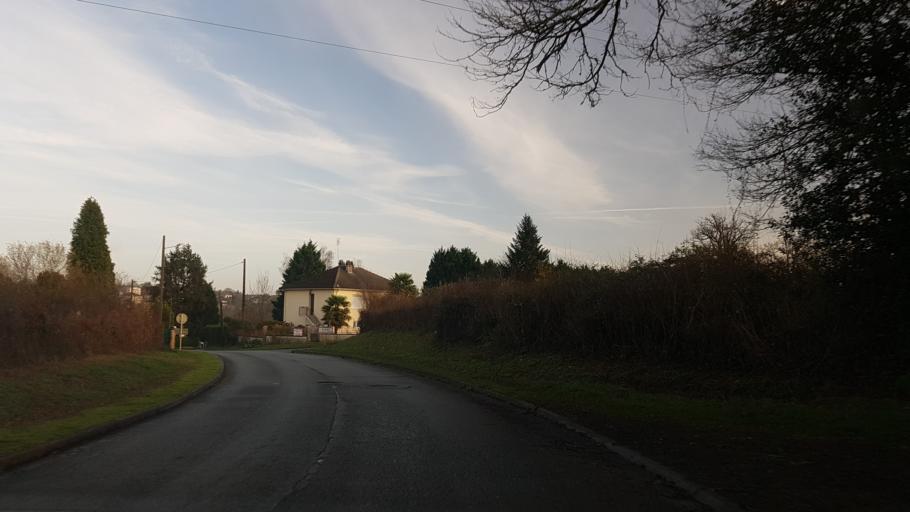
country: FR
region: Limousin
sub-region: Departement de la Haute-Vienne
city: Saint-Junien
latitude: 45.8926
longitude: 0.8798
